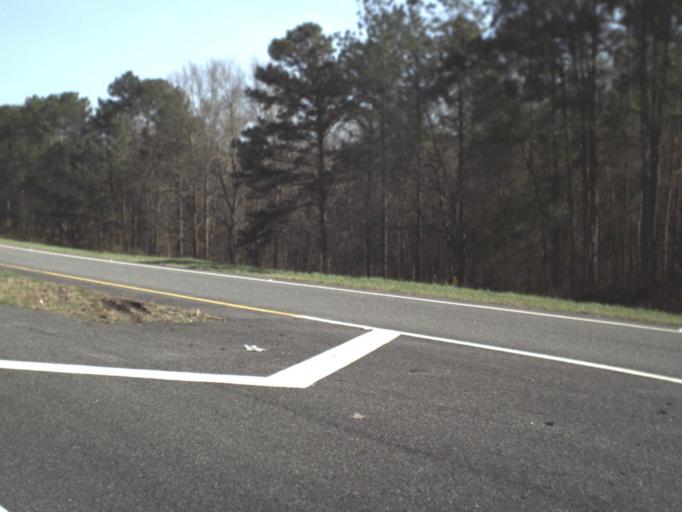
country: US
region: Florida
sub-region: Gadsden County
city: Quincy
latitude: 30.5396
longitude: -84.5997
